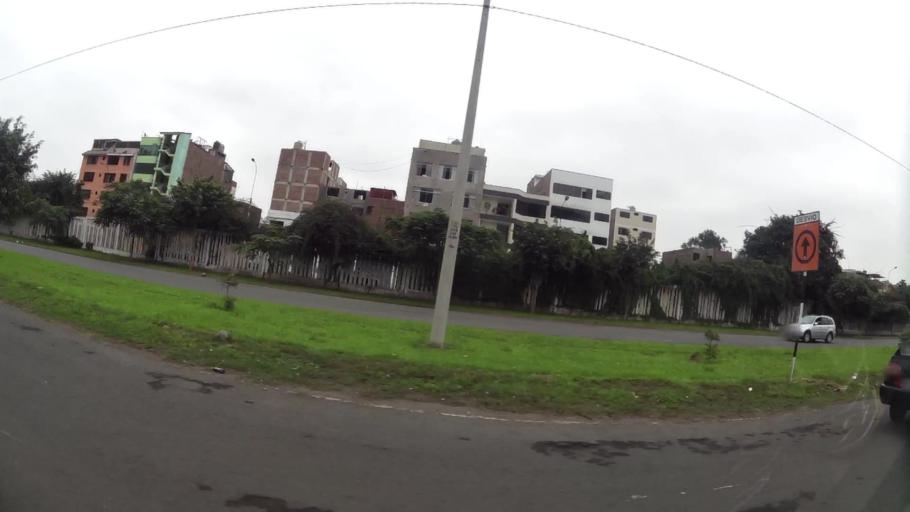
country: PE
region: Lima
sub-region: Lima
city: Vitarte
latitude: -12.0556
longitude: -76.9379
